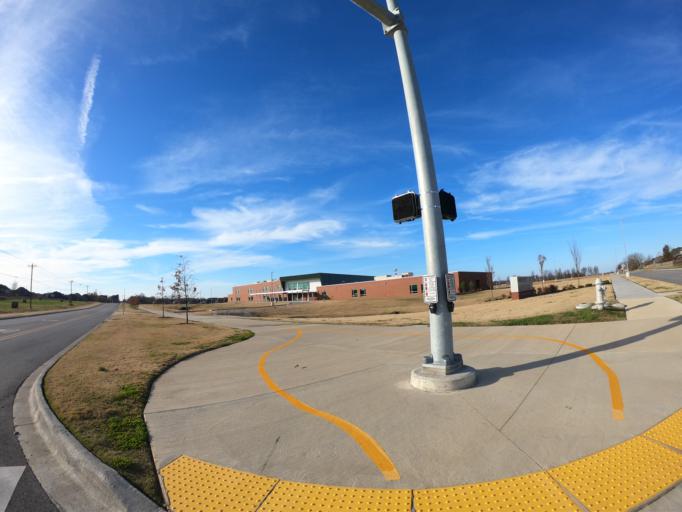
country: US
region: Arkansas
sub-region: Benton County
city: Lowell
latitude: 36.2691
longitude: -94.1637
